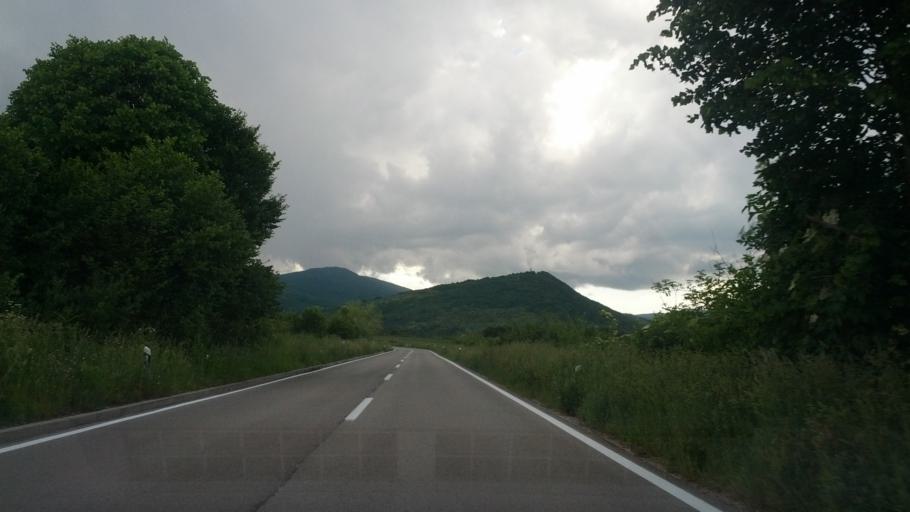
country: BA
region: Federation of Bosnia and Herzegovina
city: Izacic
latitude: 44.8785
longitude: 15.7494
